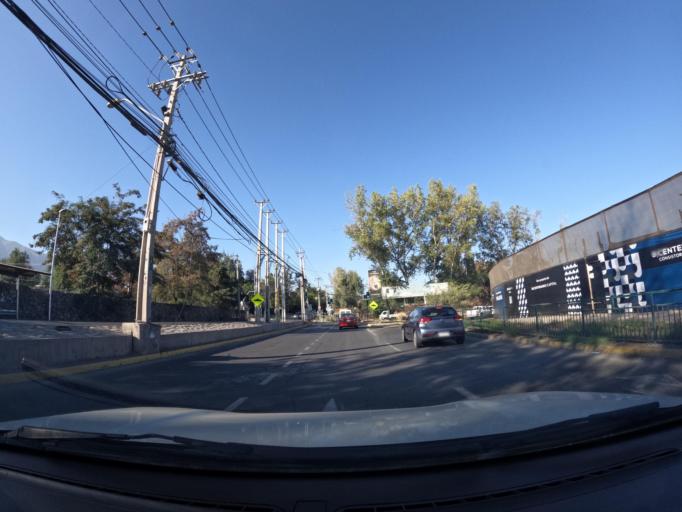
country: CL
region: Santiago Metropolitan
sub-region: Provincia de Santiago
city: Villa Presidente Frei, Nunoa, Santiago, Chile
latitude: -33.4996
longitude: -70.5523
